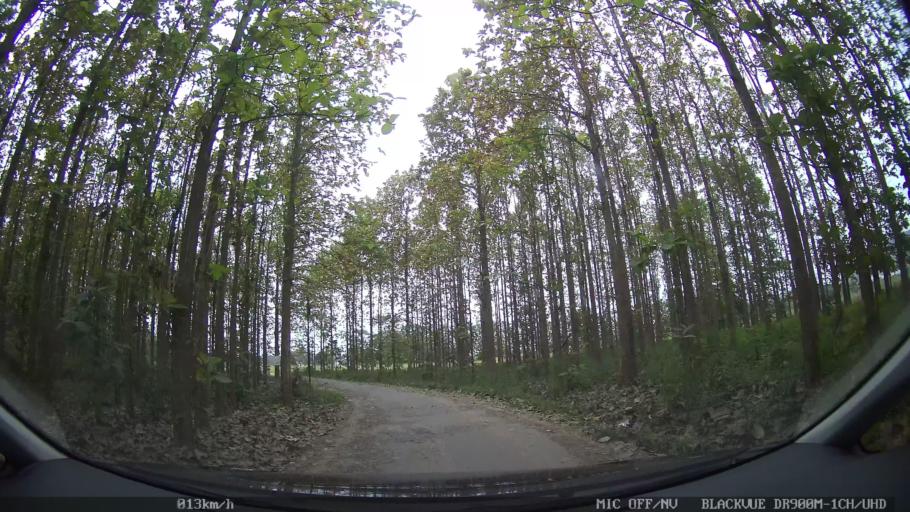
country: ID
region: Lampung
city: Panjang
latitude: -5.4068
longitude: 105.3573
